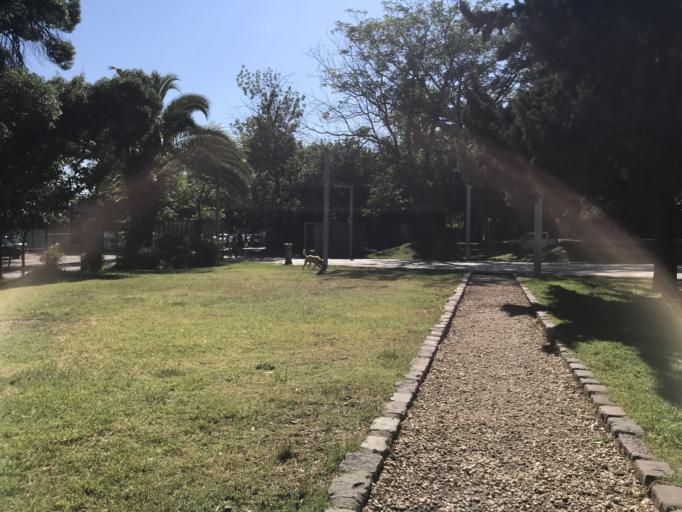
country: AR
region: Mendoza
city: Mendoza
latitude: -32.8879
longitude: -68.8319
